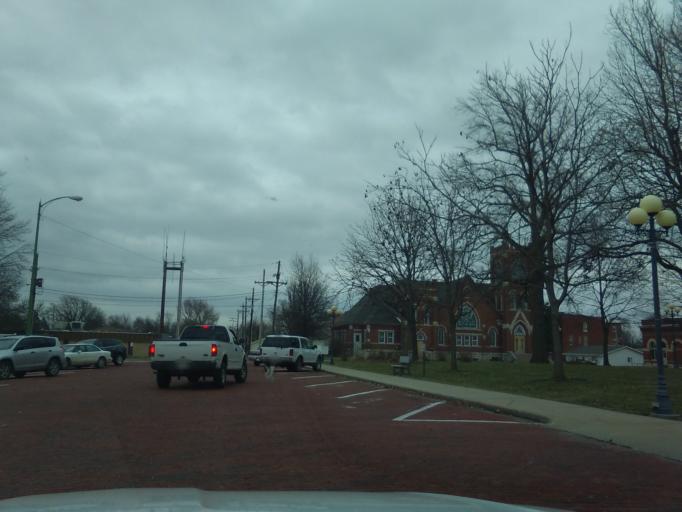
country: US
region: Nebraska
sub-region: Nemaha County
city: Auburn
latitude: 40.3861
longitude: -95.8448
